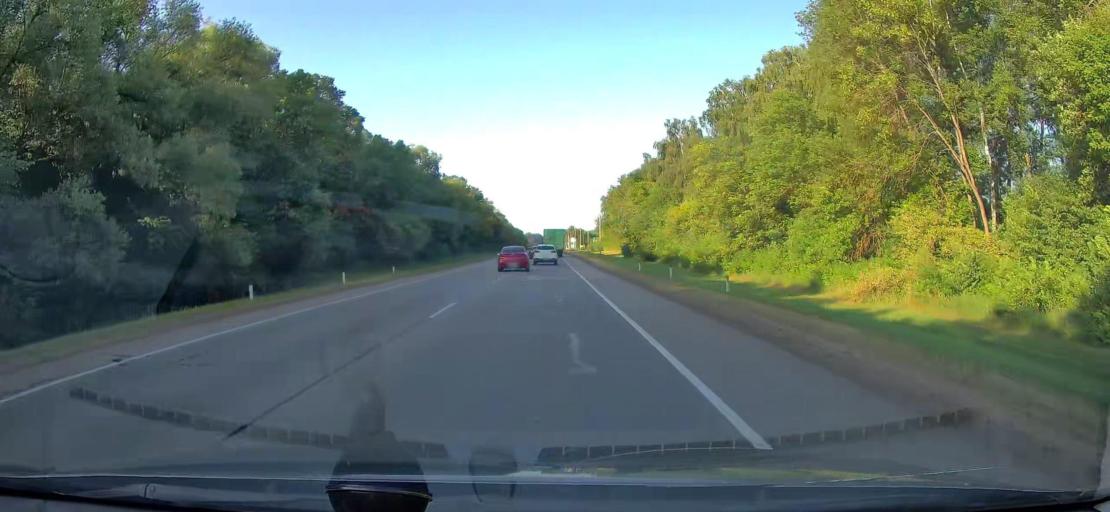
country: RU
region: Tula
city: Plavsk
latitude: 53.5893
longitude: 37.1543
